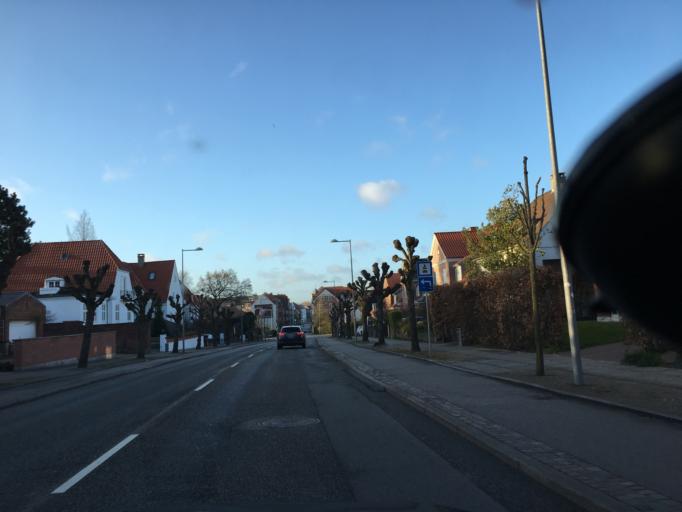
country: DK
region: North Denmark
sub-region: Alborg Kommune
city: Aalborg
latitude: 57.0485
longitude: 9.9033
